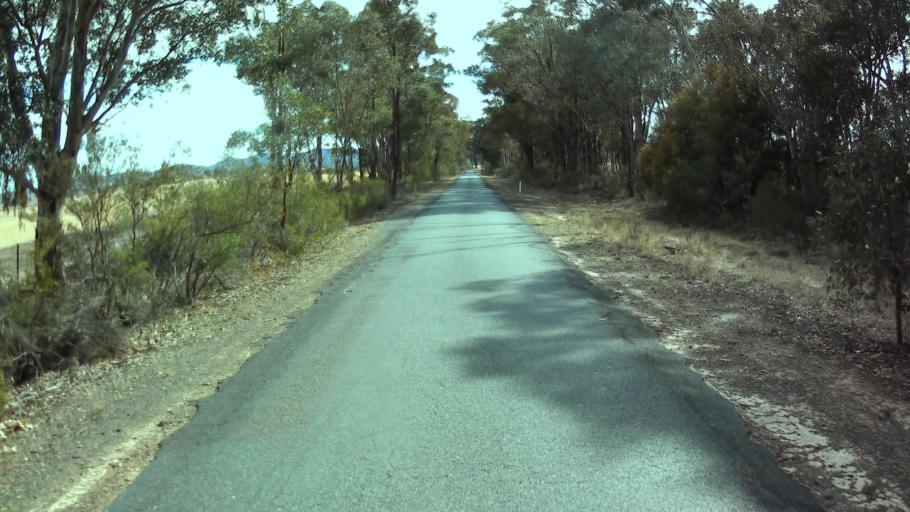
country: AU
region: New South Wales
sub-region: Weddin
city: Grenfell
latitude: -33.8532
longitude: 148.2187
